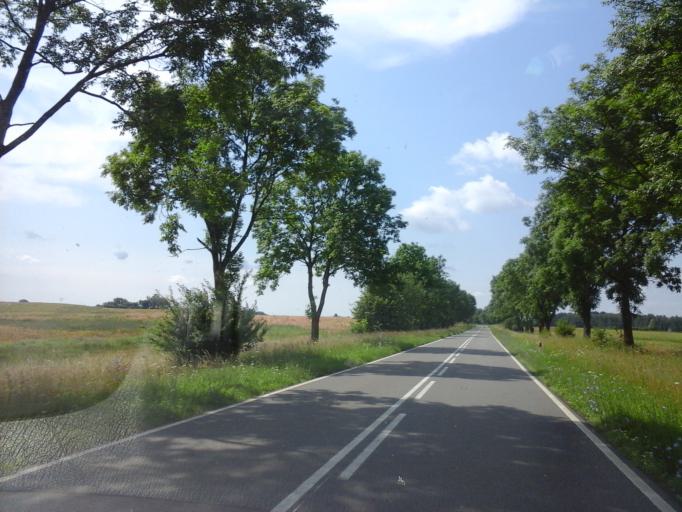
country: PL
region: West Pomeranian Voivodeship
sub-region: Powiat choszczenski
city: Recz
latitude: 53.3061
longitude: 15.5615
